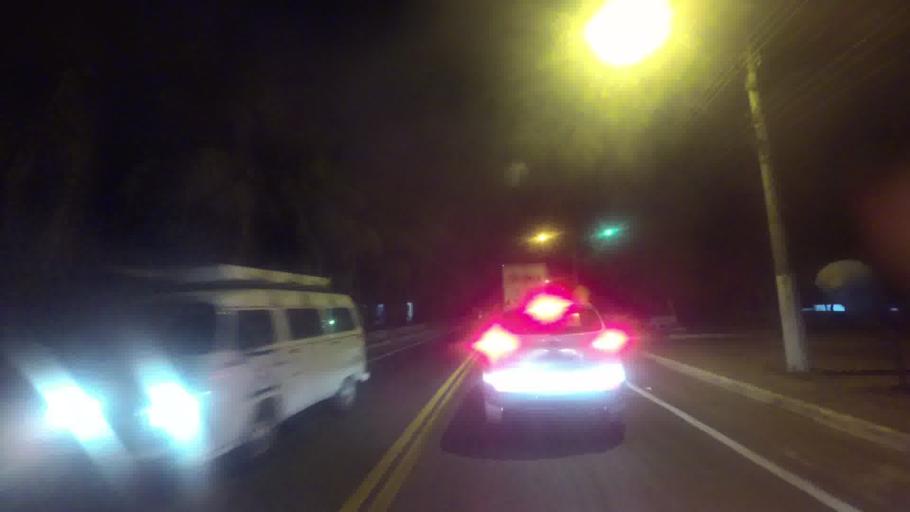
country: BR
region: Rio de Janeiro
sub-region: Sapucaia
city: Sapucaia
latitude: -22.0076
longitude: -42.9403
